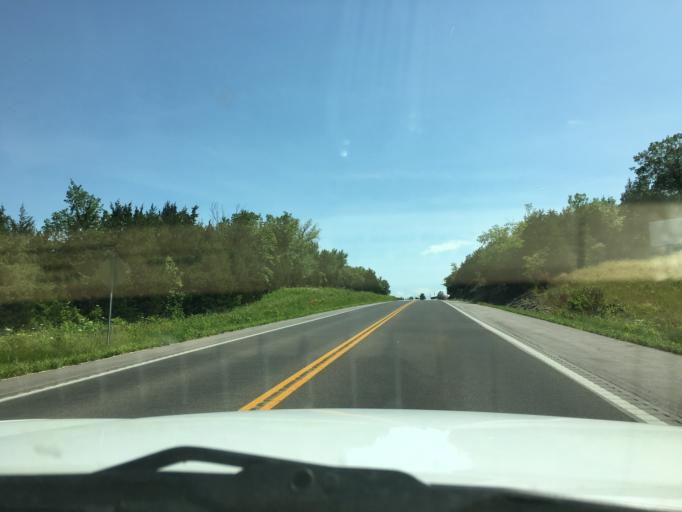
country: US
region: Missouri
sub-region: Franklin County
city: Union
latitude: 38.4950
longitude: -91.0035
